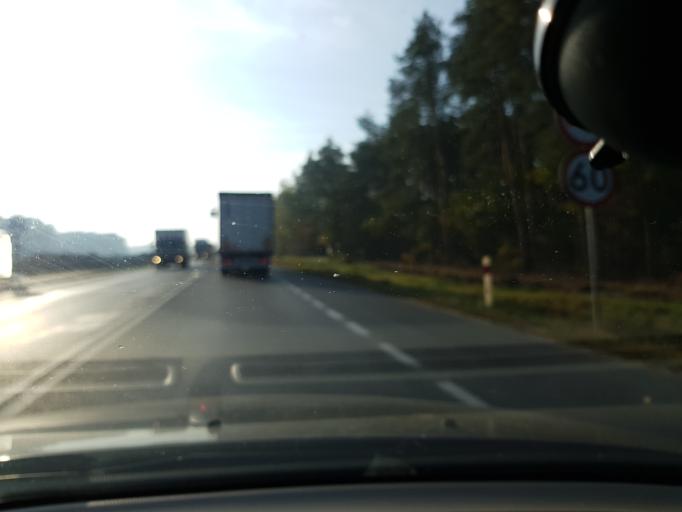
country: PL
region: Masovian Voivodeship
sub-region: Powiat otwocki
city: Otwock
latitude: 52.1556
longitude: 21.3106
